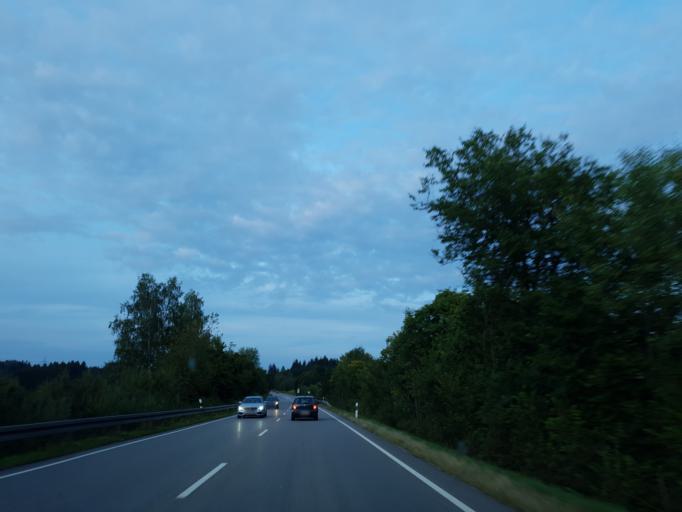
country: DE
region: Bavaria
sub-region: Swabia
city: Biessenhofen
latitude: 47.8124
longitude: 10.6567
